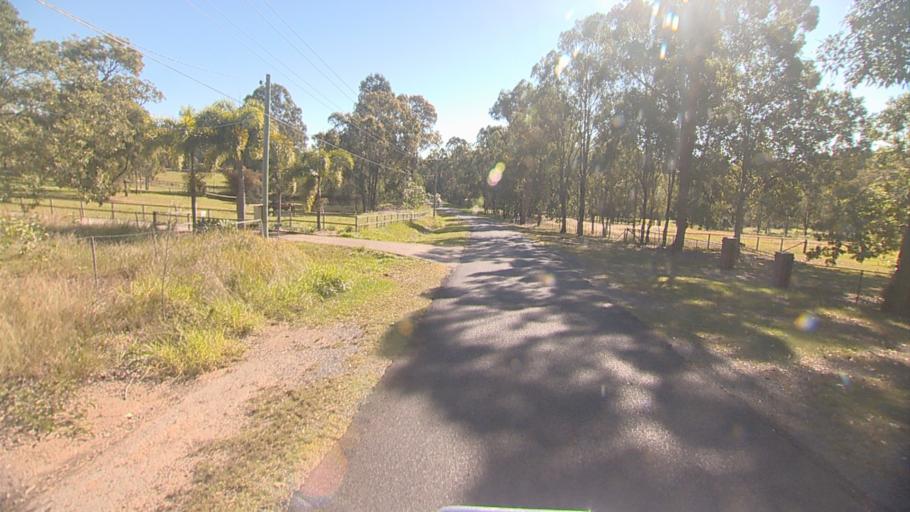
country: AU
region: Queensland
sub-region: Logan
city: Logan Reserve
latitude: -27.7353
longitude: 153.1212
